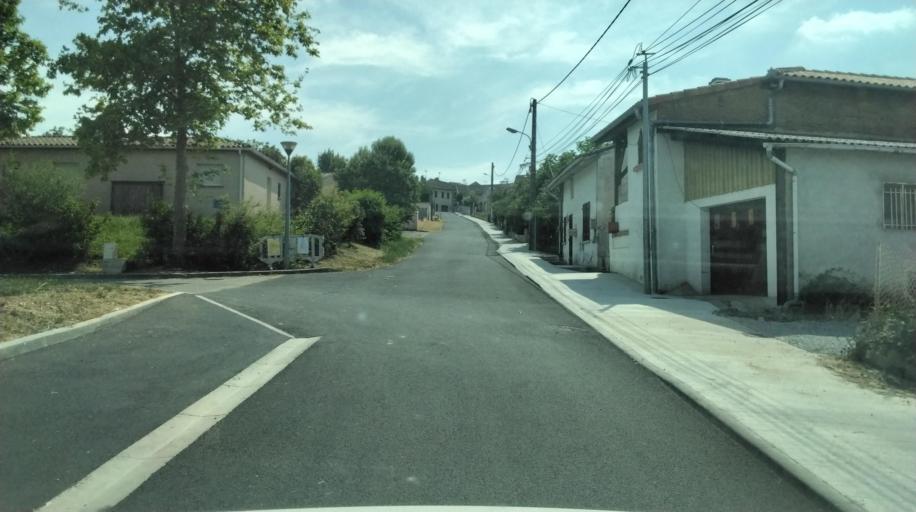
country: FR
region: Midi-Pyrenees
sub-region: Departement de la Haute-Garonne
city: Rieumes
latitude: 43.4139
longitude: 1.1250
